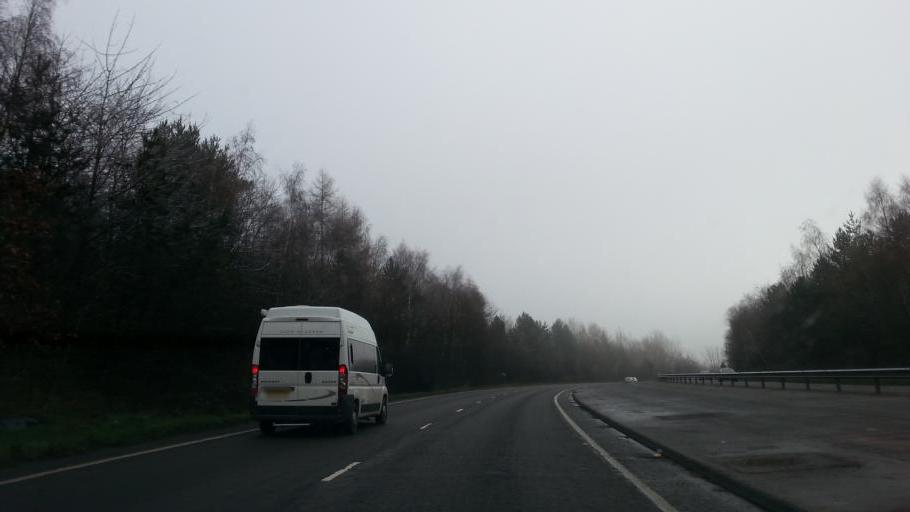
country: GB
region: England
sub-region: Cheshire East
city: Wilmslow
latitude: 53.3312
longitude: -2.2227
